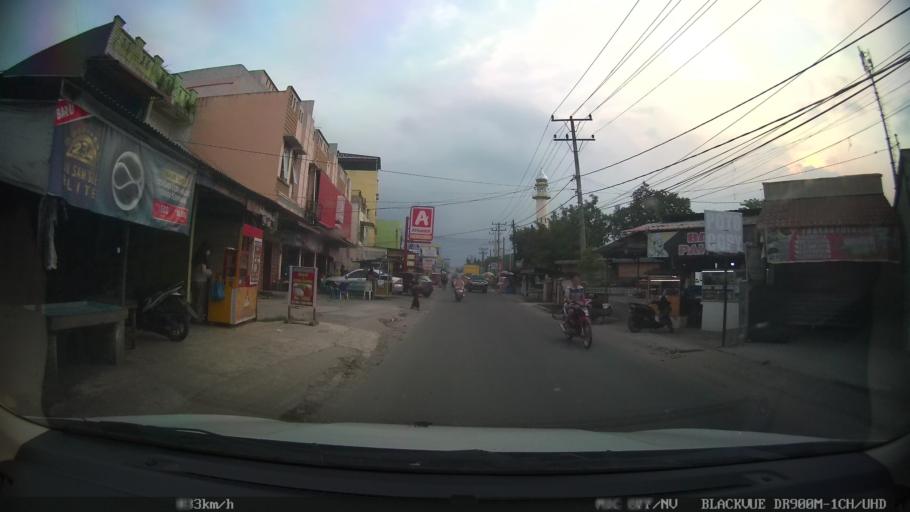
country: ID
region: North Sumatra
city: Sunggal
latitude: 3.5891
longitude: 98.6015
